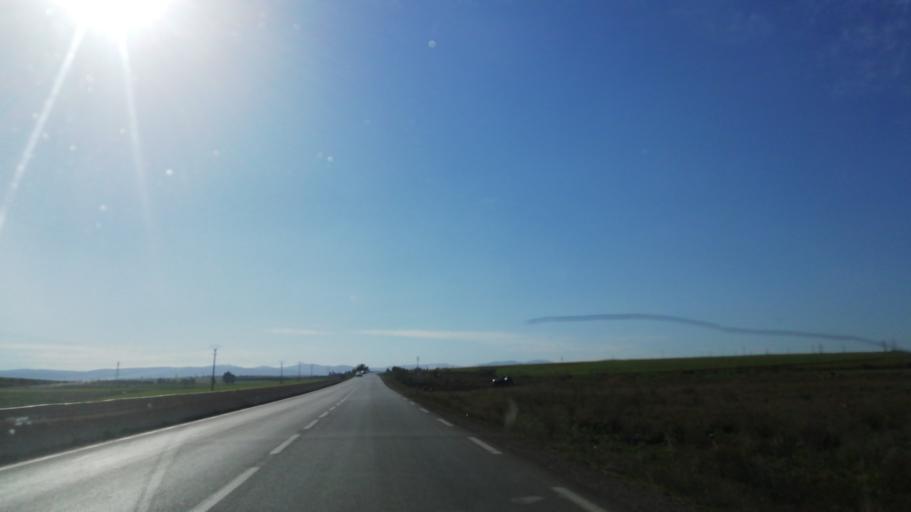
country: DZ
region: Tlemcen
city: Ouled Mimoun
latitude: 35.0016
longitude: -0.9072
